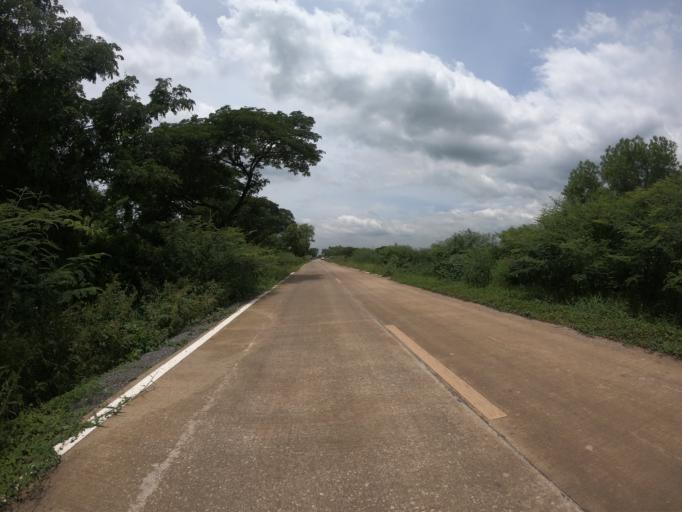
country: TH
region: Pathum Thani
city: Ban Lam Luk Ka
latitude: 13.9832
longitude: 100.8532
